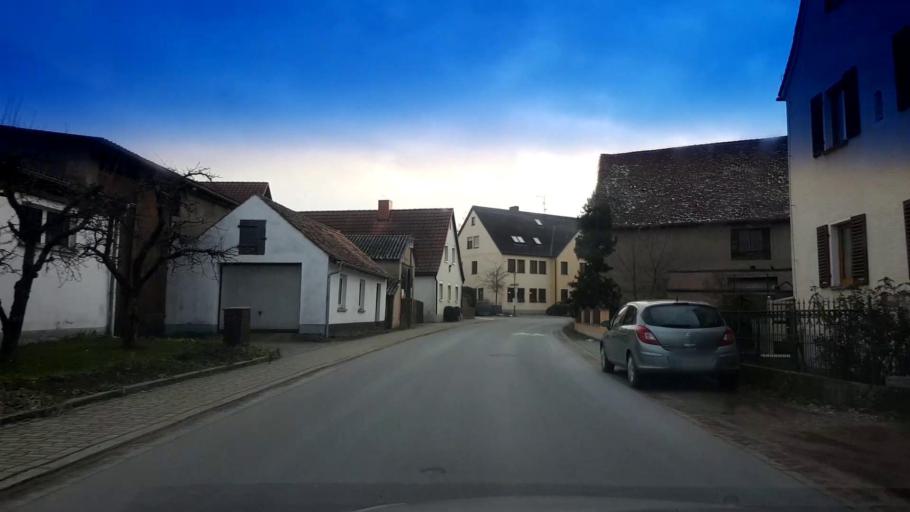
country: DE
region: Bavaria
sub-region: Upper Franconia
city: Hallerndorf
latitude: 49.7862
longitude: 10.9573
